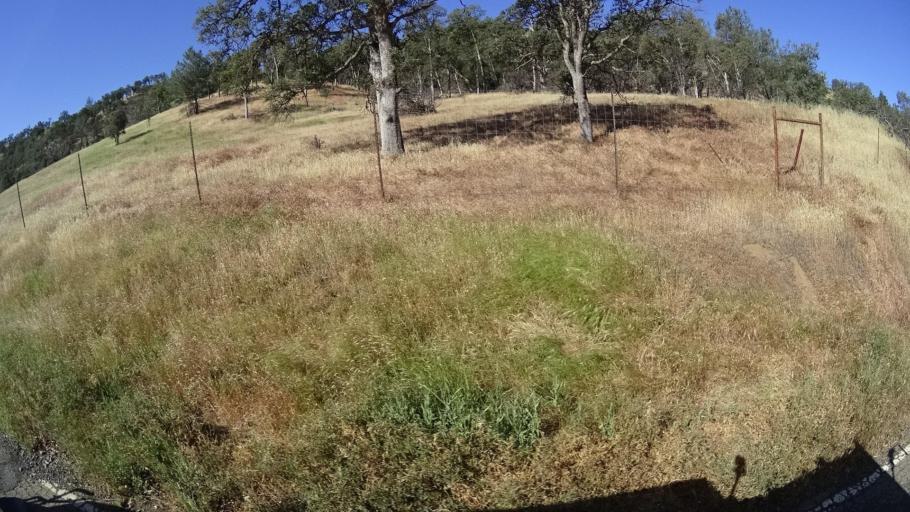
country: US
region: California
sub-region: Lake County
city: Clearlake Oaks
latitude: 38.9796
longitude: -122.6712
